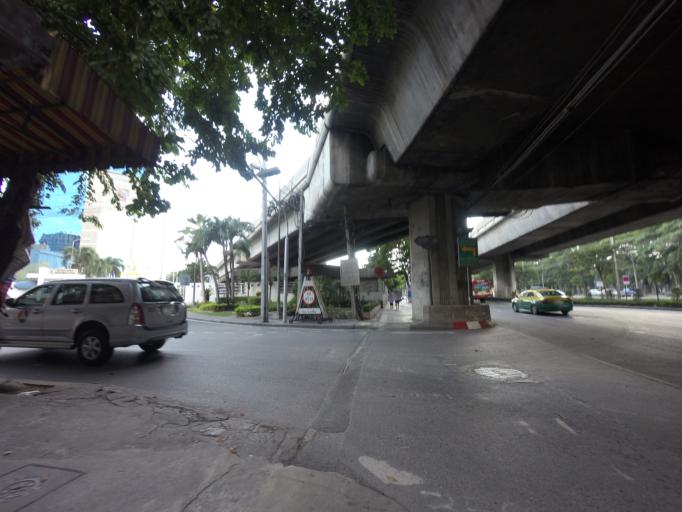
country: TH
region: Bangkok
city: Bang Sue
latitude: 13.8057
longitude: 100.5558
